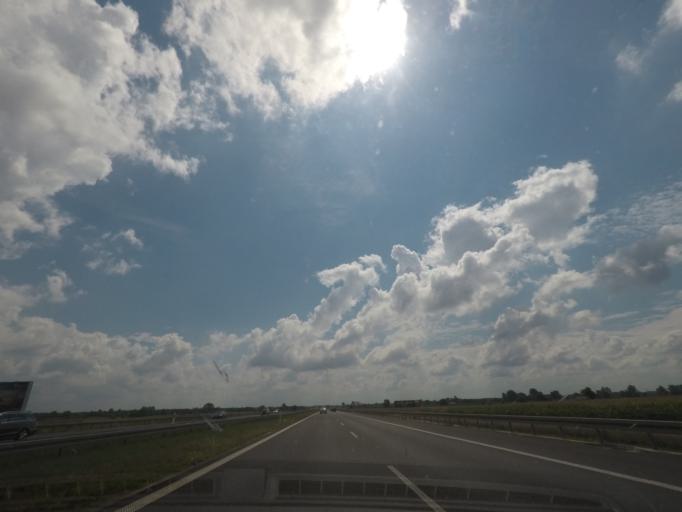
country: PL
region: Lodz Voivodeship
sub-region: Powiat zgierski
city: Strykow
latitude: 51.9696
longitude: 19.5775
